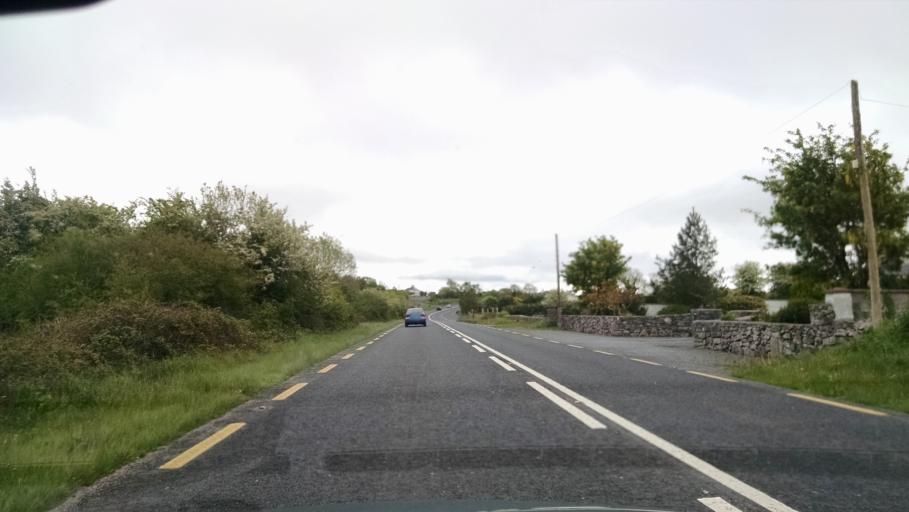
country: IE
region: Connaught
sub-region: County Galway
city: Claregalway
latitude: 53.4131
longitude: -9.0219
